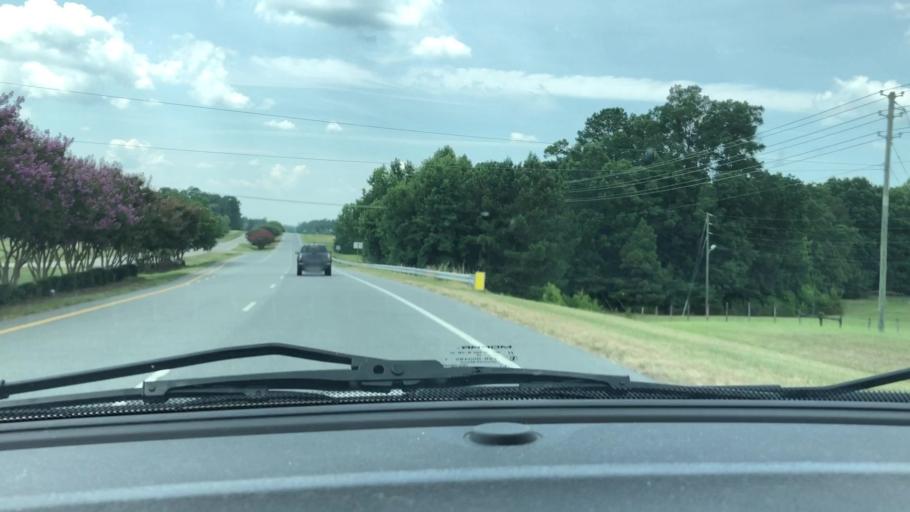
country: US
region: North Carolina
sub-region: Lee County
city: Sanford
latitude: 35.5169
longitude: -79.2169
